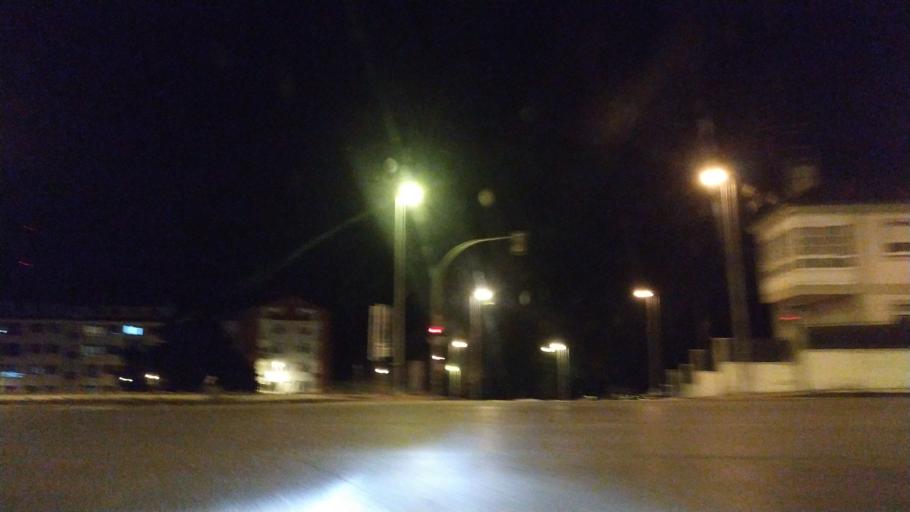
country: ES
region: Galicia
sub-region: Provincia de Lugo
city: Lugo
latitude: 42.9923
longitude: -7.5514
